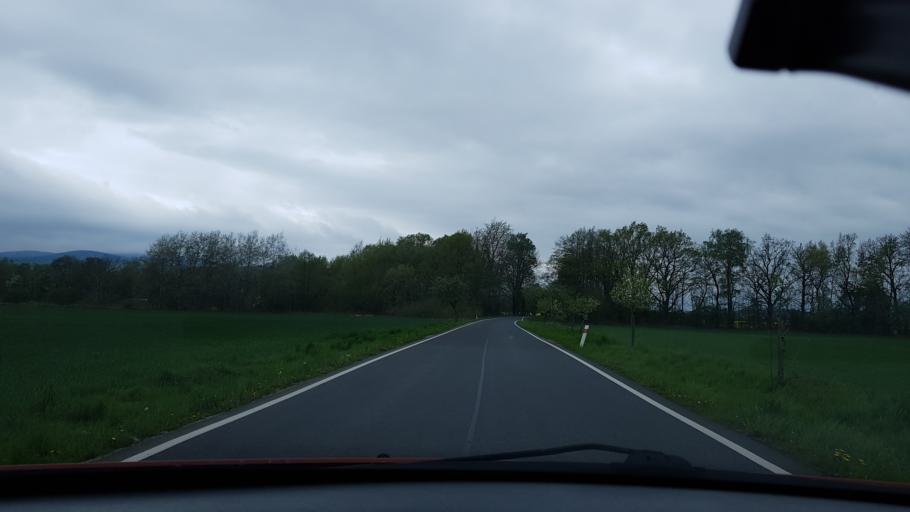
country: CZ
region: Olomoucky
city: Javornik
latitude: 50.3868
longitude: 17.0375
